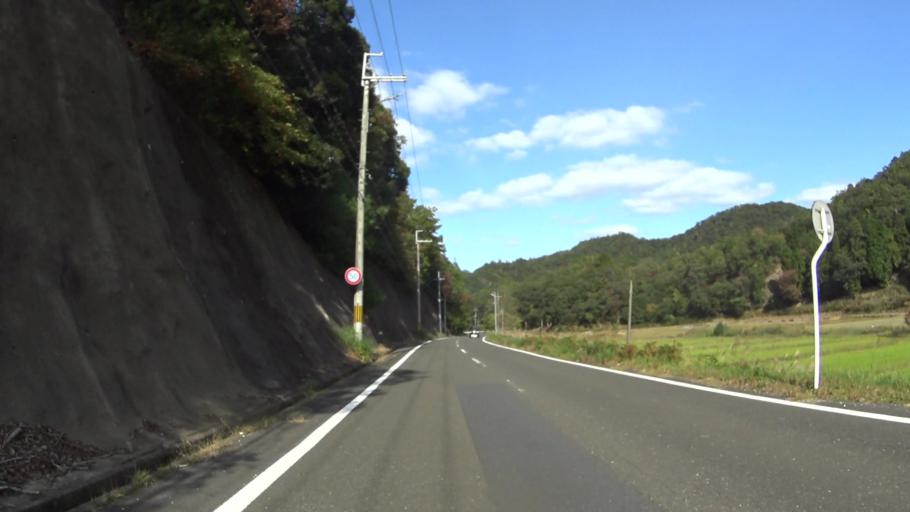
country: JP
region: Hyogo
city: Toyooka
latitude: 35.5566
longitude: 134.9784
